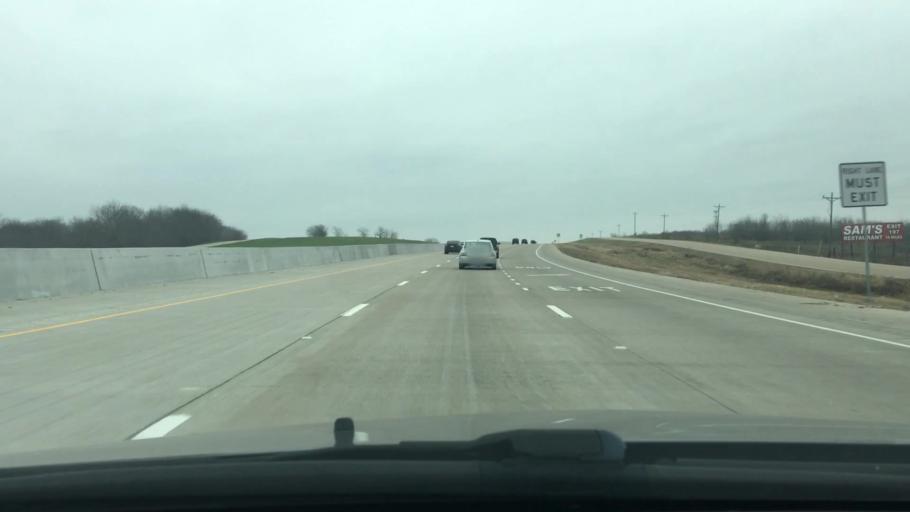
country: US
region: Texas
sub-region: Freestone County
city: Wortham
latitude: 31.8884
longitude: -96.3537
